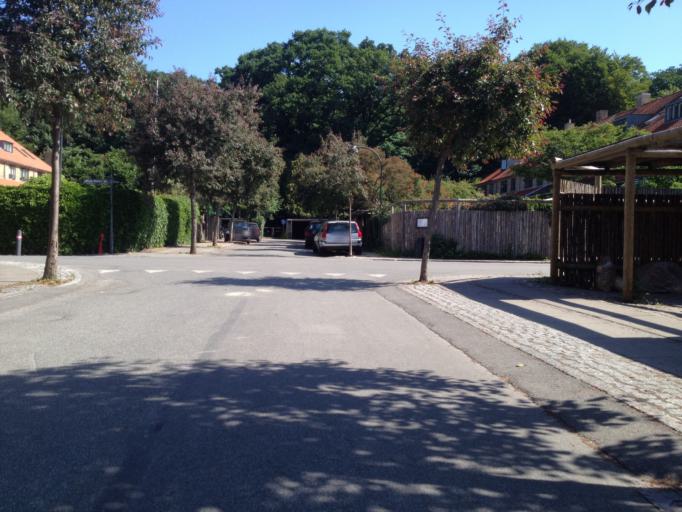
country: DK
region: Capital Region
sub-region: Gentofte Kommune
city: Charlottenlund
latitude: 55.7455
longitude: 12.5791
